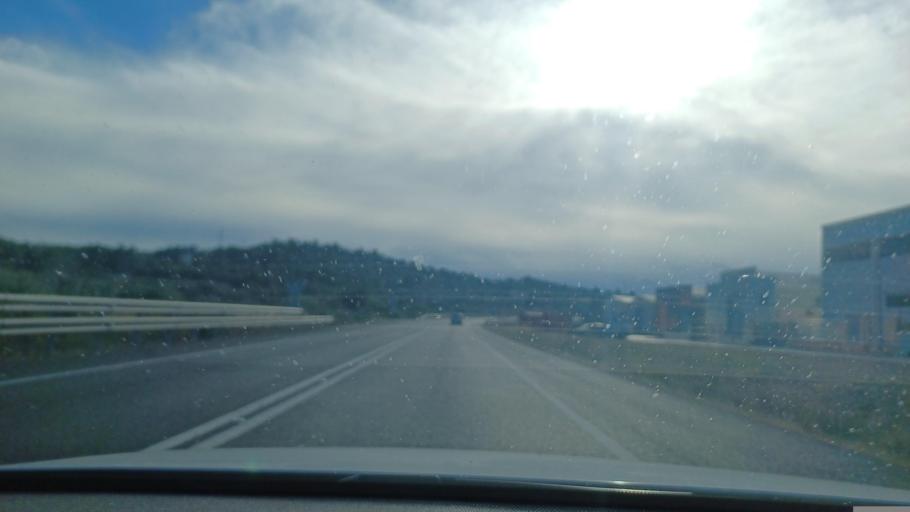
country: ES
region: Catalonia
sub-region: Provincia de Tarragona
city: El Perello
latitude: 40.8800
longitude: 0.7182
